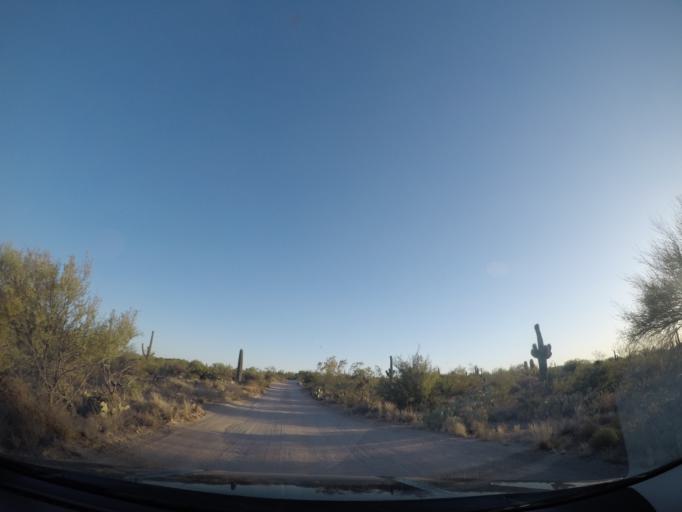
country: US
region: Arizona
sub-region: Pima County
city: Tanque Verde
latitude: 32.2093
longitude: -110.7262
